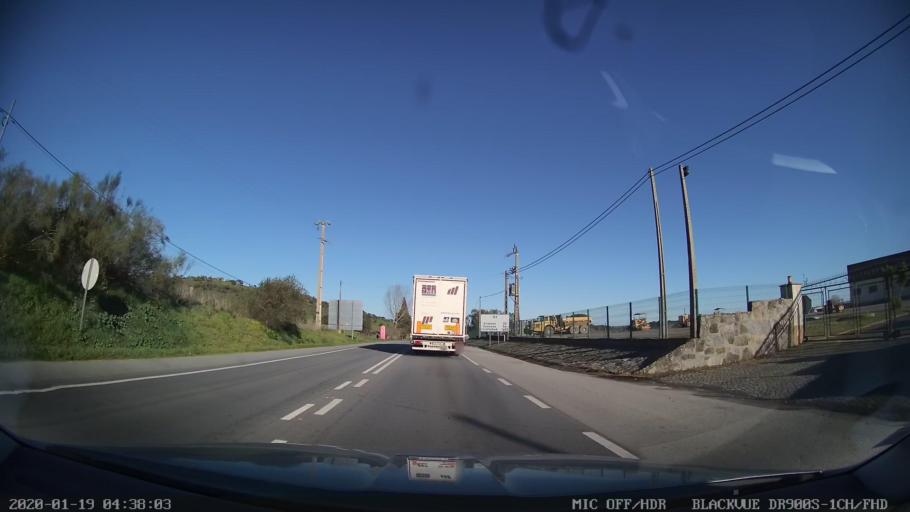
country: PT
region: Evora
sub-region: Montemor-O-Novo
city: Montemor-o-Novo
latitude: 38.6474
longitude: -8.1993
